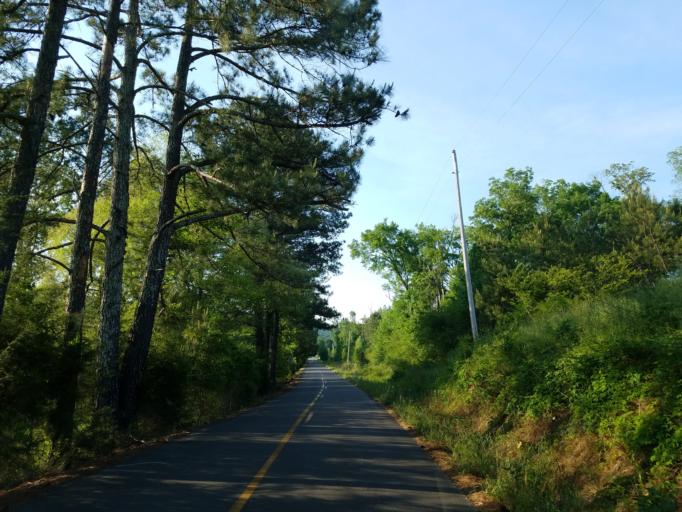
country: US
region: Georgia
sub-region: Gordon County
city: Calhoun
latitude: 34.5401
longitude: -85.1076
